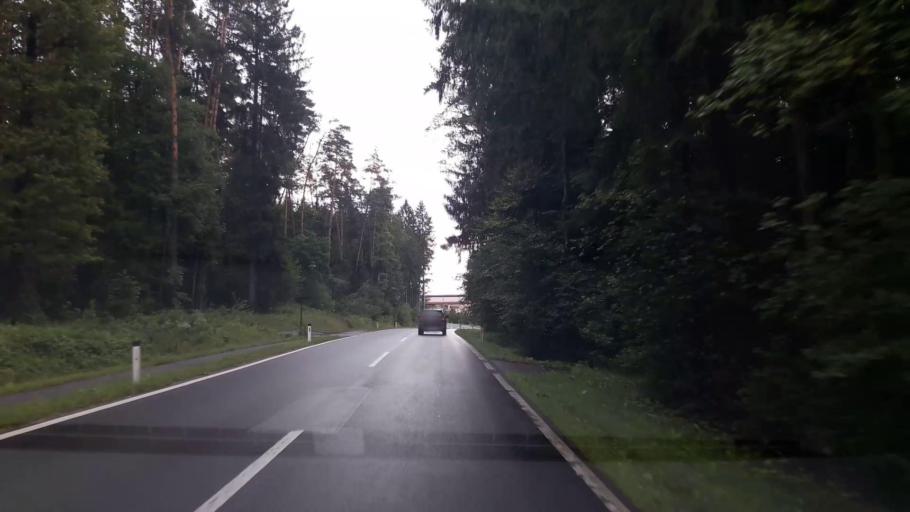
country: AT
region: Styria
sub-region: Politischer Bezirk Hartberg-Fuerstenfeld
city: Kaindorf
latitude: 47.2166
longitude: 15.9173
